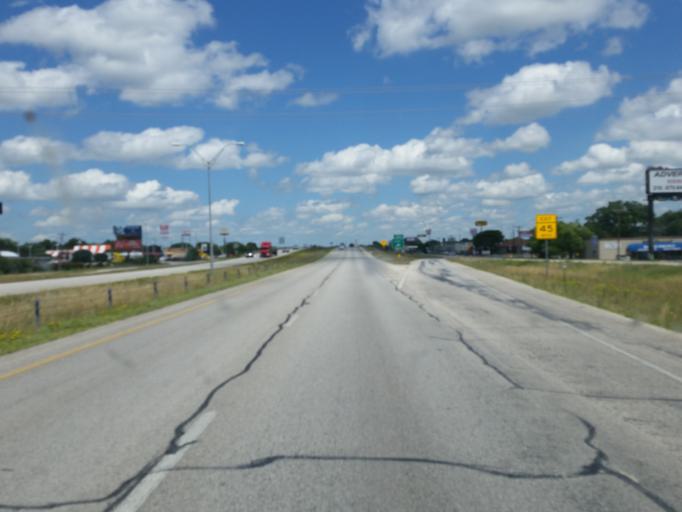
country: US
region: Texas
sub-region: Callahan County
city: Clyde
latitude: 32.4127
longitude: -99.4944
